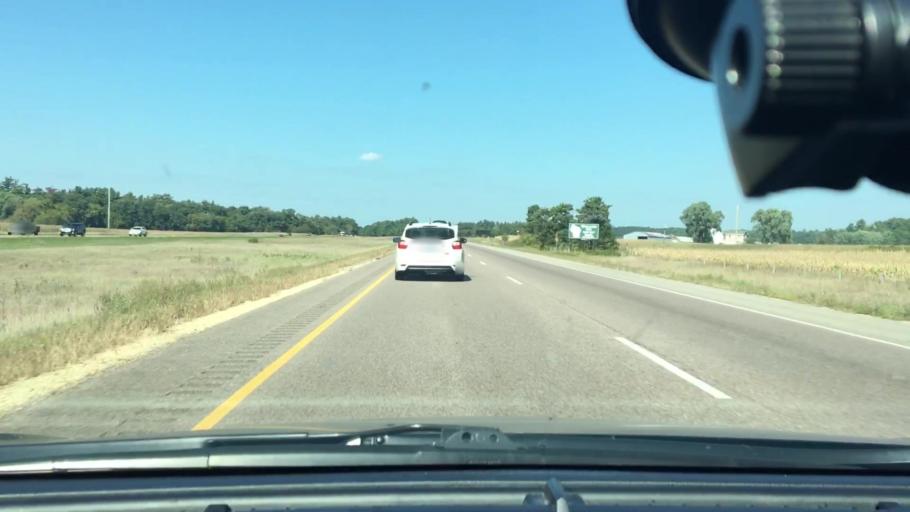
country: US
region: Wisconsin
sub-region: Eau Claire County
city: Altoona
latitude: 44.7399
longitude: -91.3744
